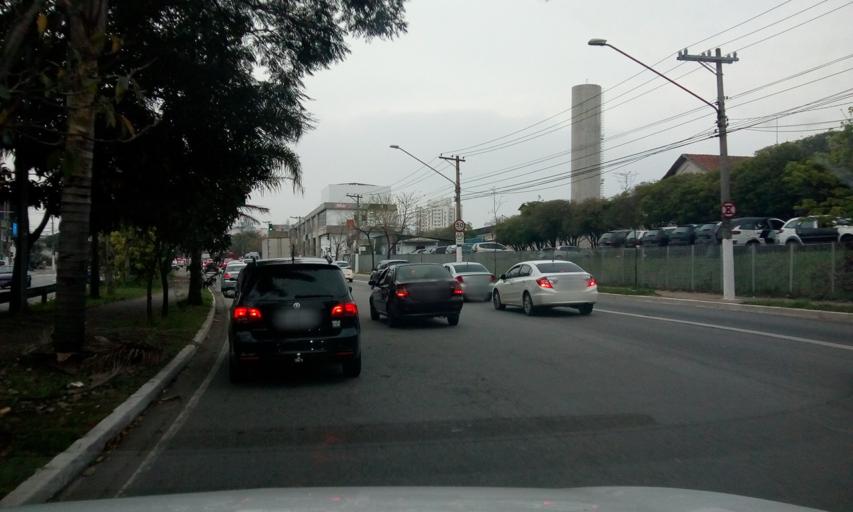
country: BR
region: Sao Paulo
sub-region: Sao Paulo
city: Sao Paulo
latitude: -23.5027
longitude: -46.6184
